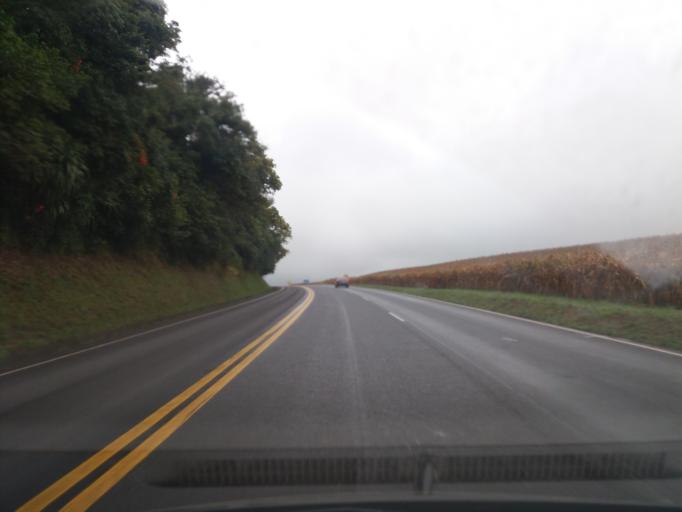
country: BR
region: Parana
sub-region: Ampere
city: Ampere
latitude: -25.9137
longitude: -53.4305
